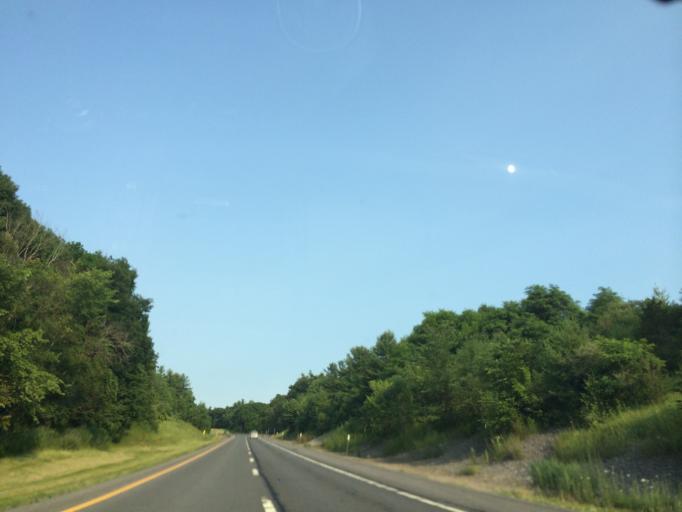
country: US
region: New York
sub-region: Rensselaer County
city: Castleton-on-Hudson
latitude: 42.4952
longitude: -73.7296
